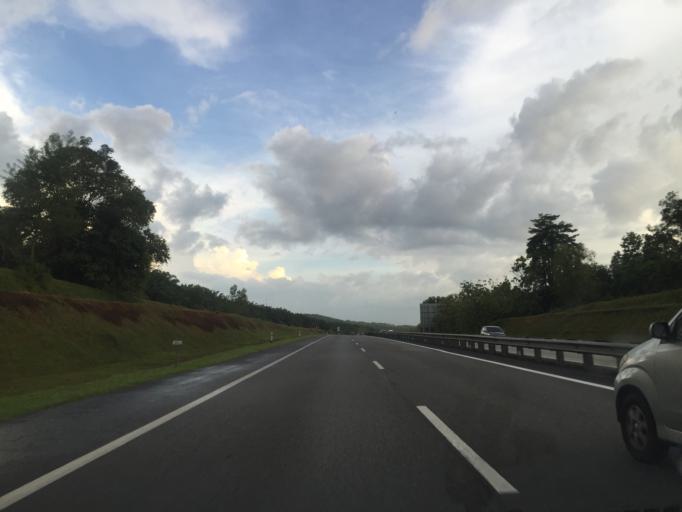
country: MY
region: Kedah
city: Gurun
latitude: 5.7938
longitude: 100.4989
